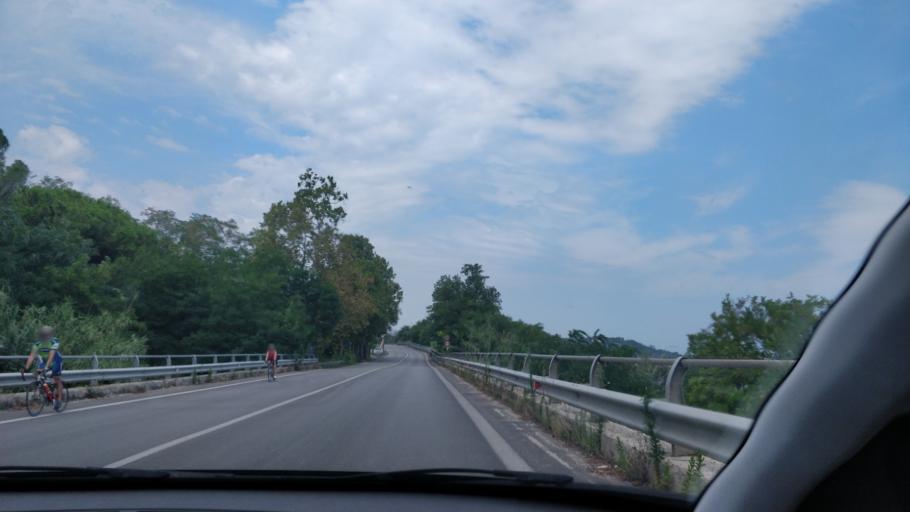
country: IT
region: Abruzzo
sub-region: Provincia di Chieti
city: Marina di San Vito
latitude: 42.3173
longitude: 14.4347
